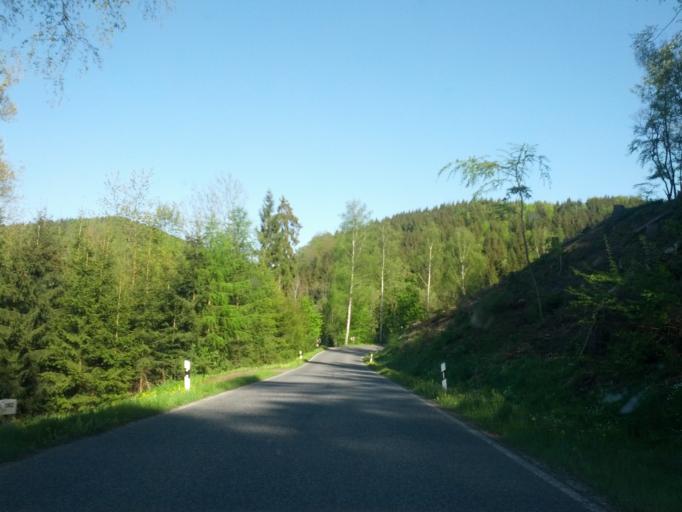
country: DE
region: Thuringia
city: Fretterode
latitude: 51.3102
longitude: 10.0209
